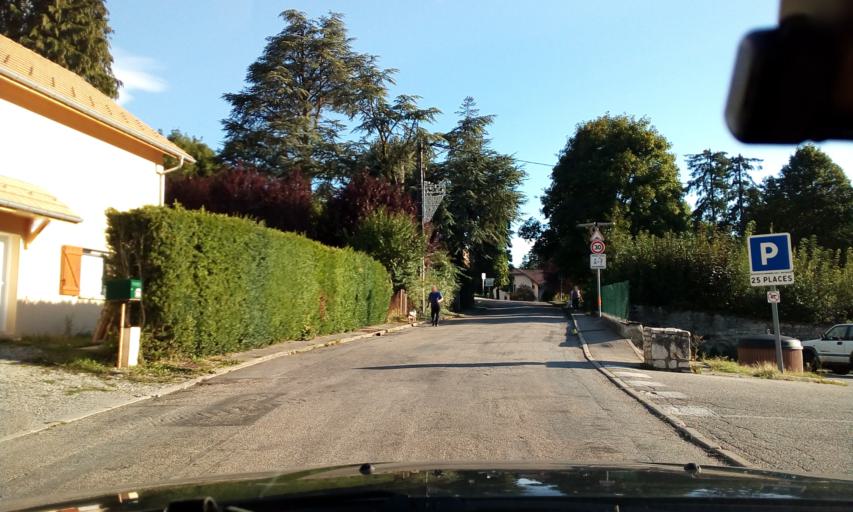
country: FR
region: Rhone-Alpes
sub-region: Departement de l'Isere
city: La Motte-Saint-Martin
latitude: 44.9175
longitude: 5.6362
